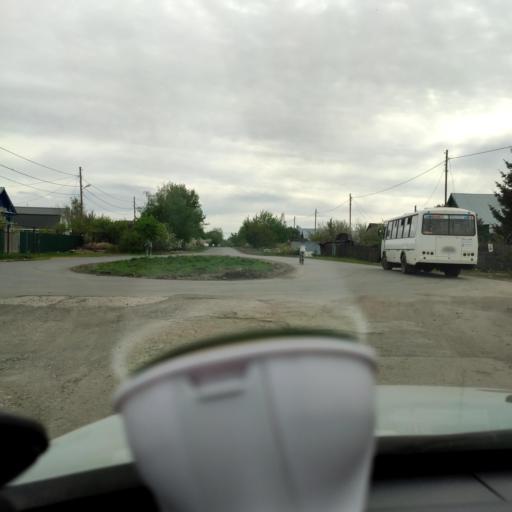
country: RU
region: Samara
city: Smyshlyayevka
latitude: 53.2224
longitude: 50.3382
